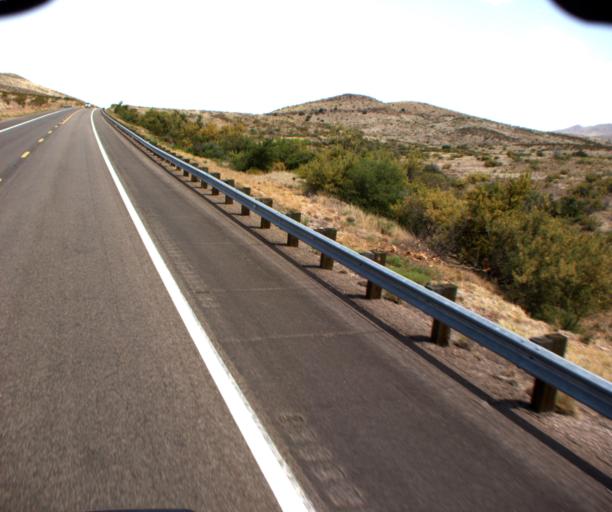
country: US
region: Arizona
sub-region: Greenlee County
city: Clifton
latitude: 32.7408
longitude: -109.2060
